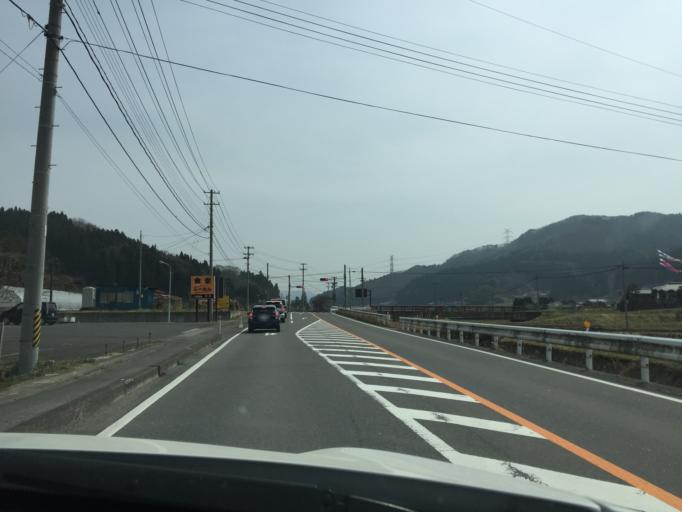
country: JP
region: Fukushima
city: Ishikawa
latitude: 37.1342
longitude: 140.4940
